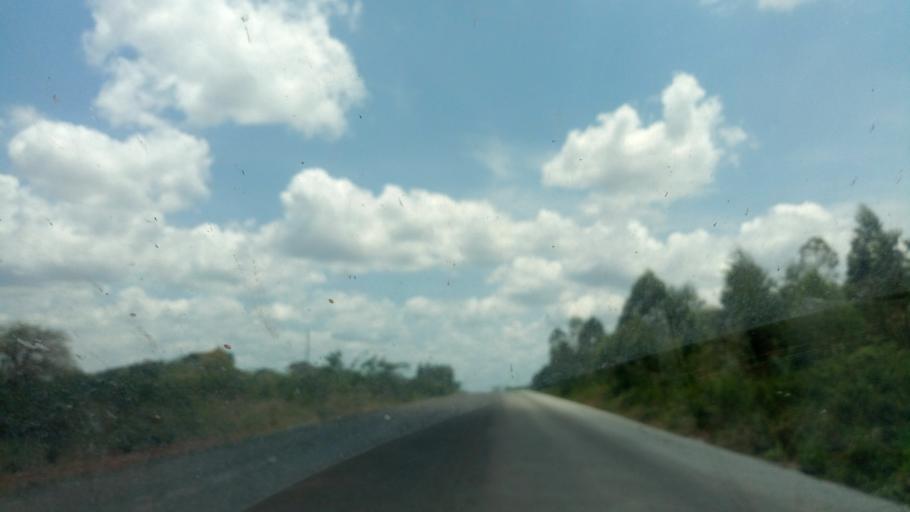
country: UG
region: Western Region
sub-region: Kiryandongo District
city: Kiryandongo
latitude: 1.7904
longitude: 31.9439
